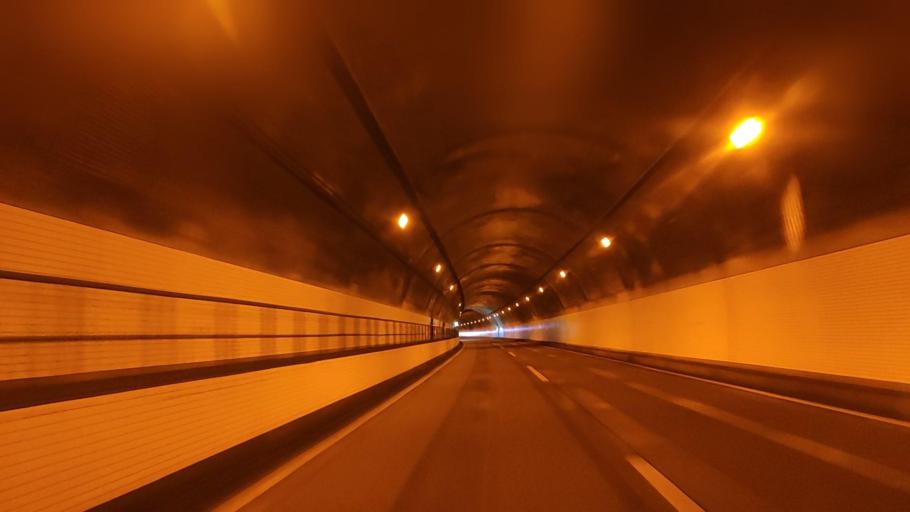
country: JP
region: Niigata
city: Itoigawa
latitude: 37.0189
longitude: 137.8371
